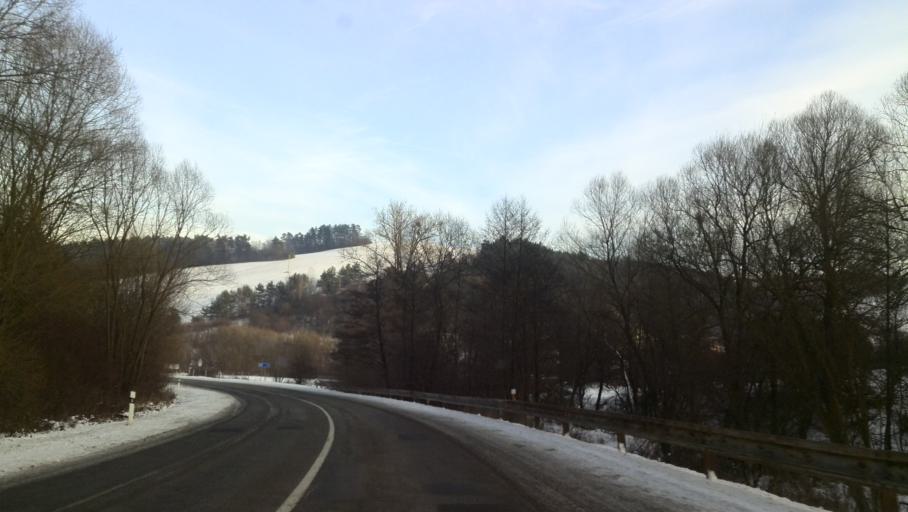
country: SK
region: Presovsky
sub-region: Okres Presov
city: Presov
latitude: 48.9587
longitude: 21.1154
